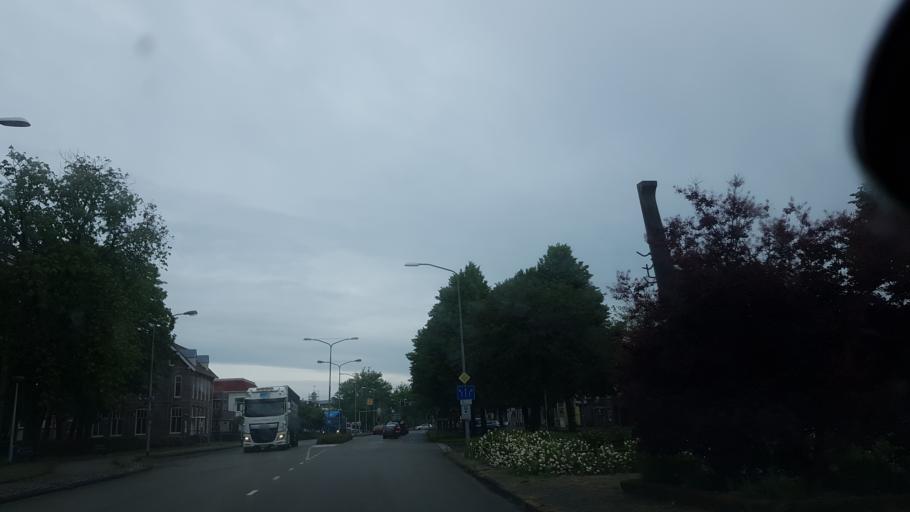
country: NL
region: Groningen
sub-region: Gemeente Hoogezand-Sappemeer
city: Hoogezand
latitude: 53.1636
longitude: 6.7531
